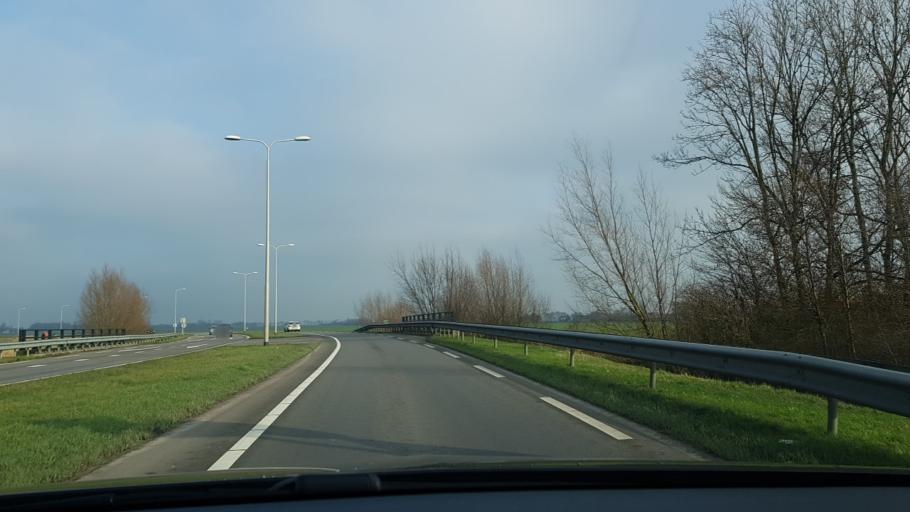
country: NL
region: North Holland
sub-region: Gemeente Uithoorn
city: Uithoorn
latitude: 52.2351
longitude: 4.8533
